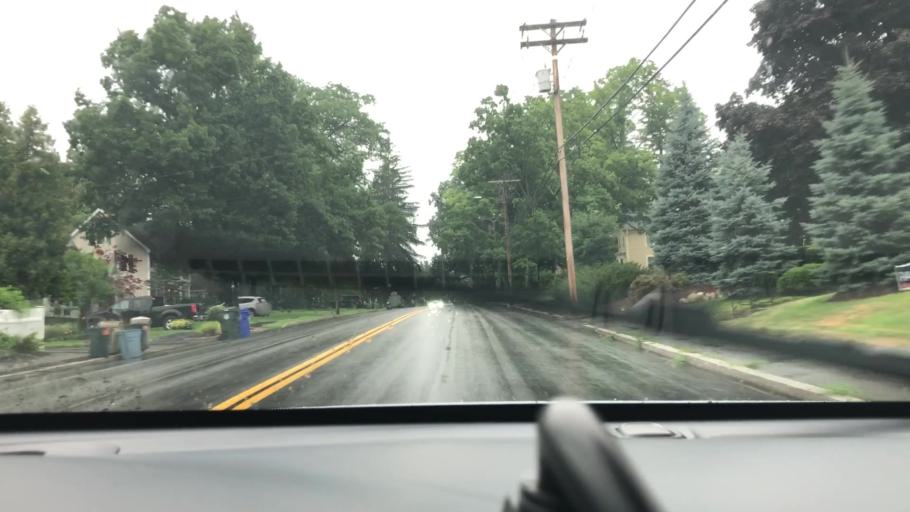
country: US
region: New Hampshire
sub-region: Hillsborough County
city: Manchester
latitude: 43.0139
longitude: -71.4614
